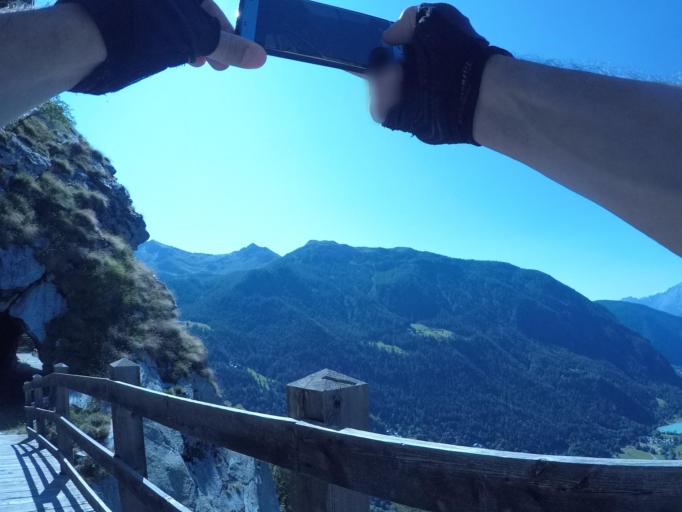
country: IT
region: Aosta Valley
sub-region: Valle d'Aosta
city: Valtournenche
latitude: 45.8775
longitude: 7.6152
